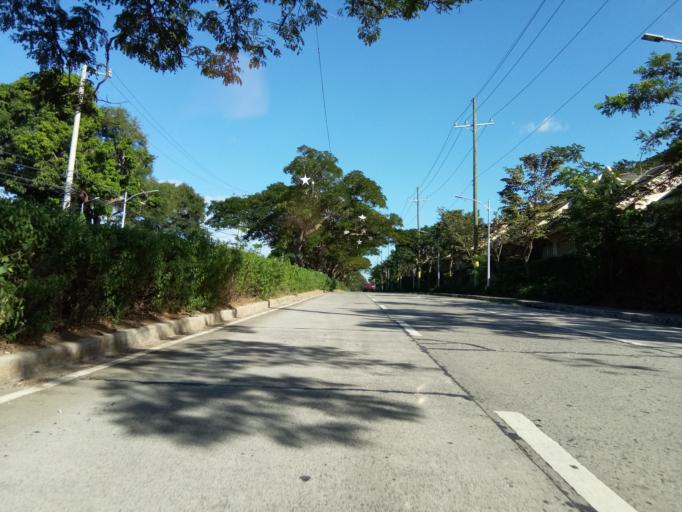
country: PH
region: Calabarzon
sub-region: Province of Cavite
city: Dasmarinas
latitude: 14.3510
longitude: 120.9584
